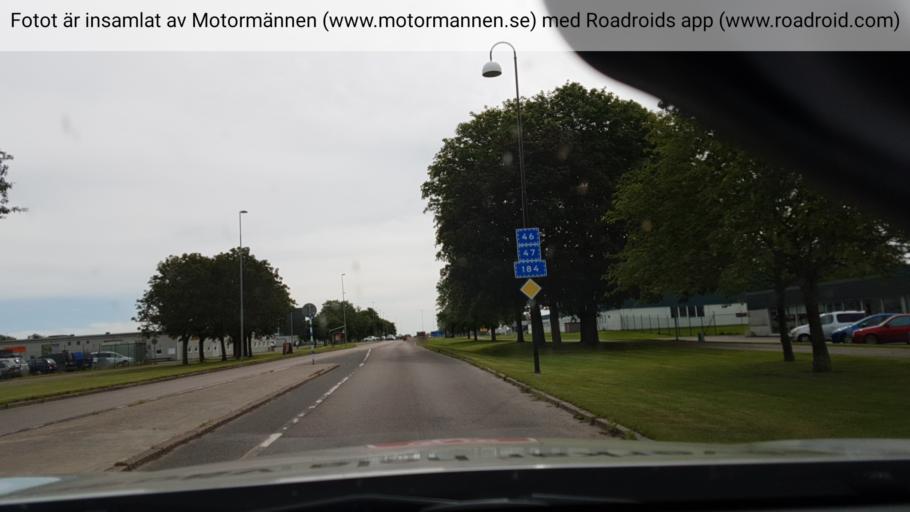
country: SE
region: Vaestra Goetaland
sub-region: Falkopings Kommun
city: Falkoeping
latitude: 58.1625
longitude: 13.5665
